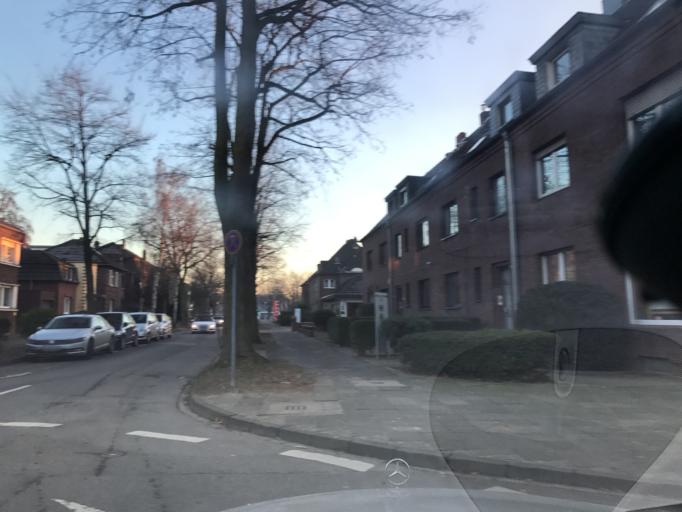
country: DE
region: North Rhine-Westphalia
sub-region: Regierungsbezirk Dusseldorf
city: Krefeld
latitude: 51.3426
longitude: 6.5980
